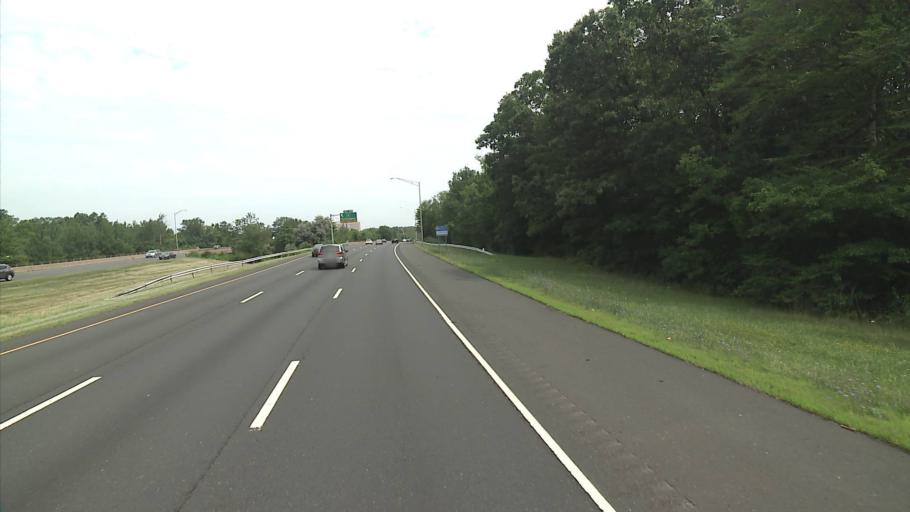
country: US
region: Connecticut
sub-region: Hartford County
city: Farmington
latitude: 41.7170
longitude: -72.7966
